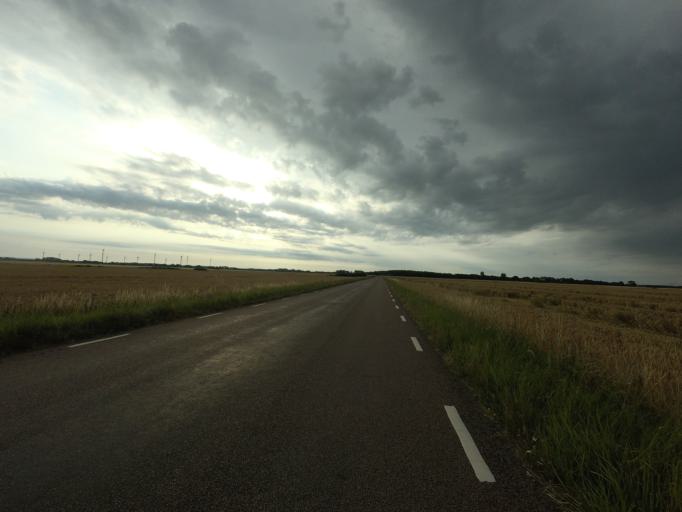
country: SE
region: Skane
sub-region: Helsingborg
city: Odakra
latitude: 56.1555
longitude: 12.7155
